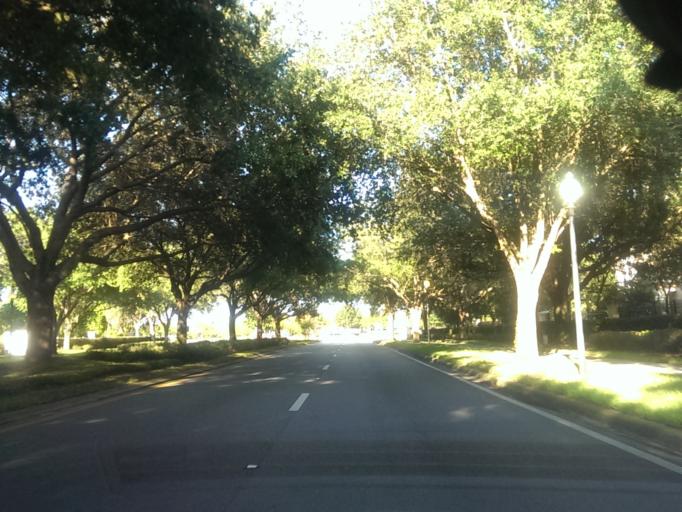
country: US
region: Florida
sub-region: Orange County
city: Williamsburg
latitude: 28.3803
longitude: -81.4889
